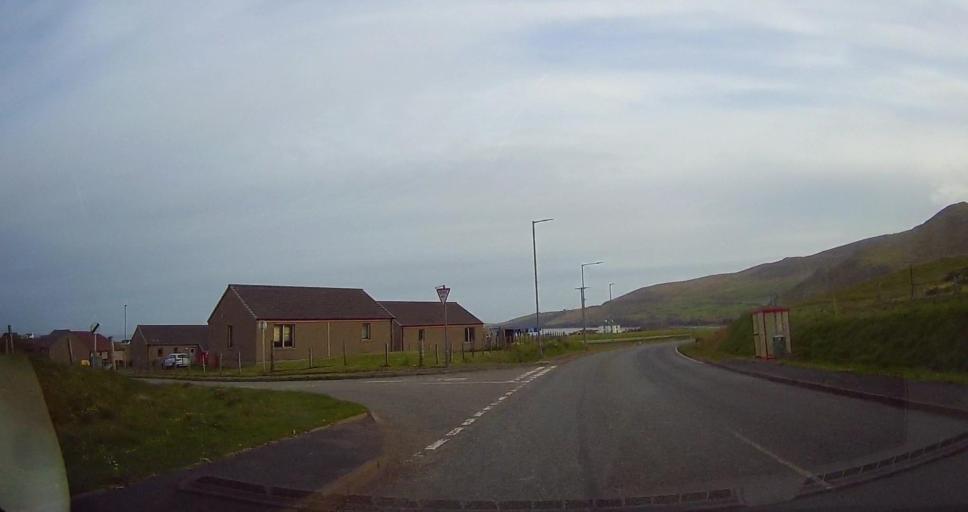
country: GB
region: Scotland
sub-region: Shetland Islands
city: Sandwick
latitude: 60.0389
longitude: -1.2296
